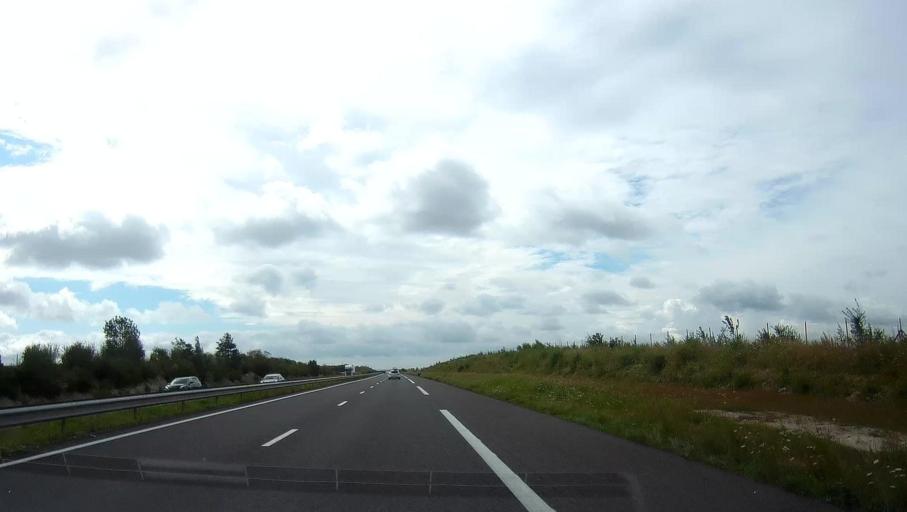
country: FR
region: Champagne-Ardenne
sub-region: Departement de la Marne
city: Fagnieres
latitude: 49.0205
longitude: 4.2906
